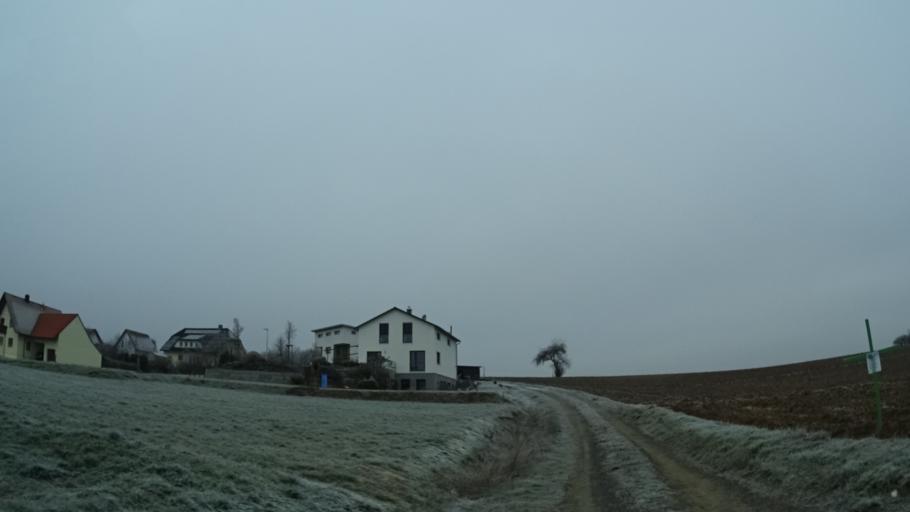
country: DE
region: Bavaria
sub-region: Regierungsbezirk Unterfranken
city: Burgpreppach
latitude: 50.1433
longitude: 10.6534
